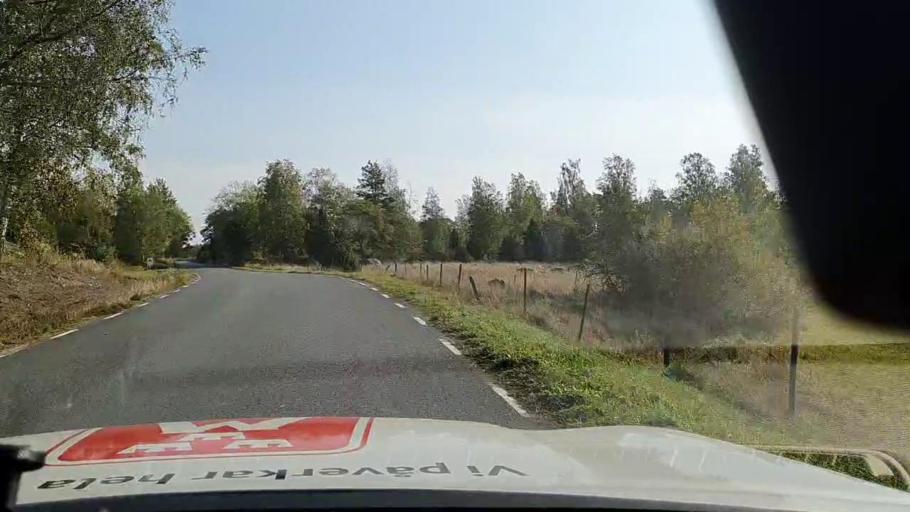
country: SE
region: Soedermanland
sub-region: Eskilstuna Kommun
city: Kvicksund
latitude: 59.3147
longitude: 16.2575
